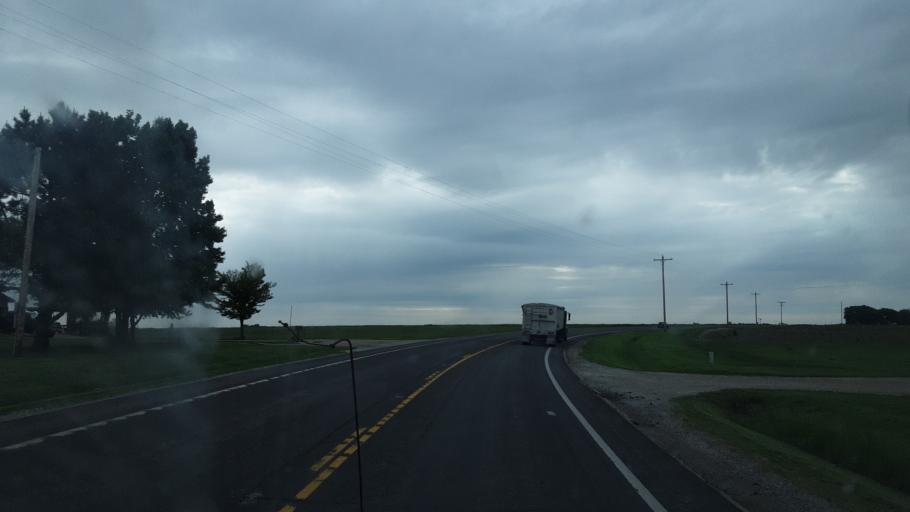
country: US
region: Illinois
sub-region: Fulton County
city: Lewistown
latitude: 40.3494
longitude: -90.2794
